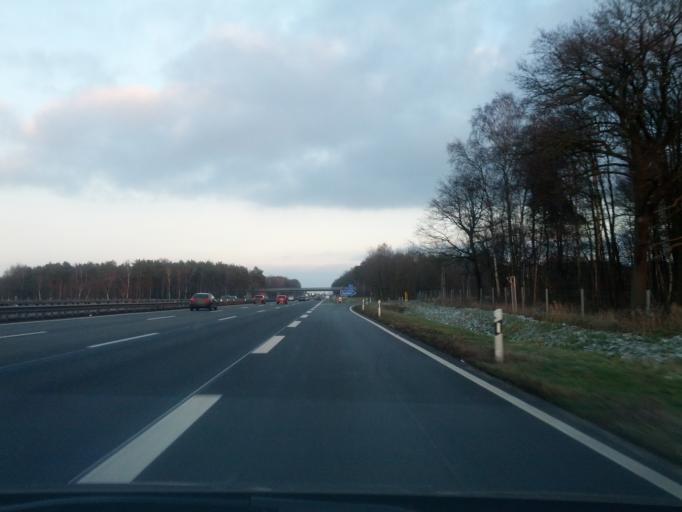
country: DE
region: Lower Saxony
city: Halvesbostel
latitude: 53.3360
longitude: 9.6296
